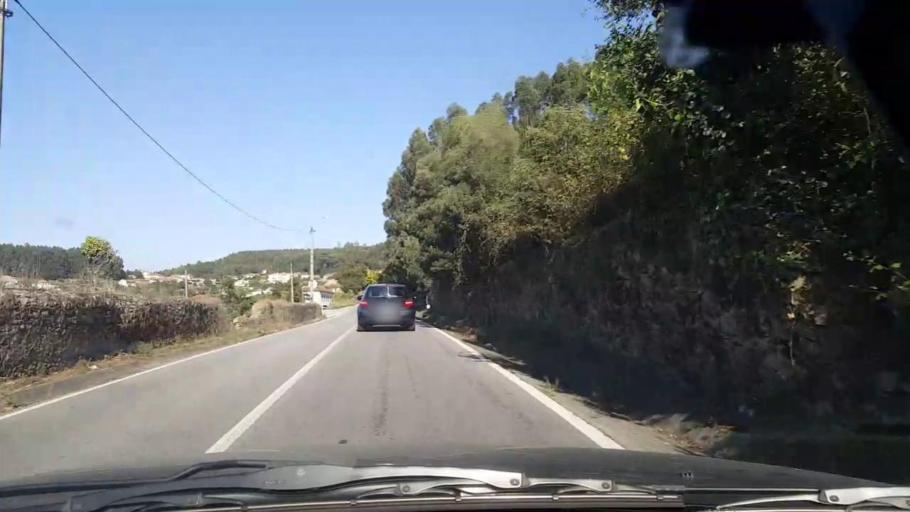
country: PT
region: Porto
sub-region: Maia
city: Gemunde
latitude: 41.3255
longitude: -8.6520
